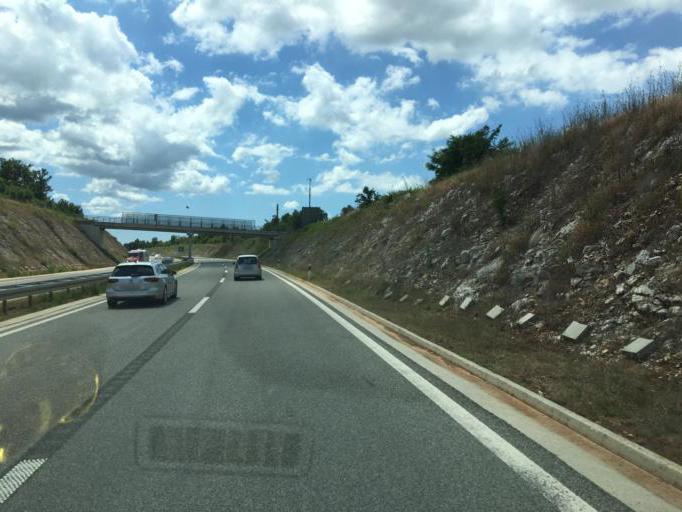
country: HR
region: Istarska
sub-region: Grad Porec
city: Porec
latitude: 45.2477
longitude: 13.7072
